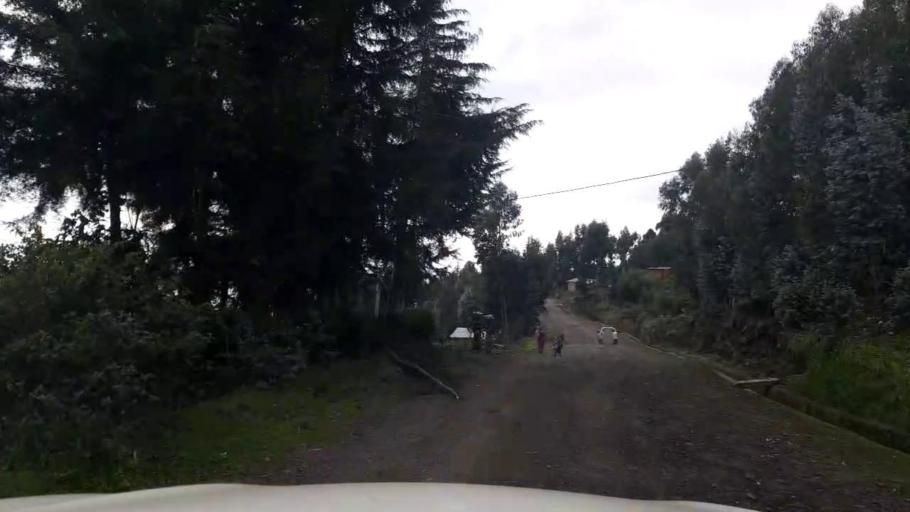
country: RW
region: Northern Province
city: Musanze
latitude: -1.4878
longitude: 29.5285
